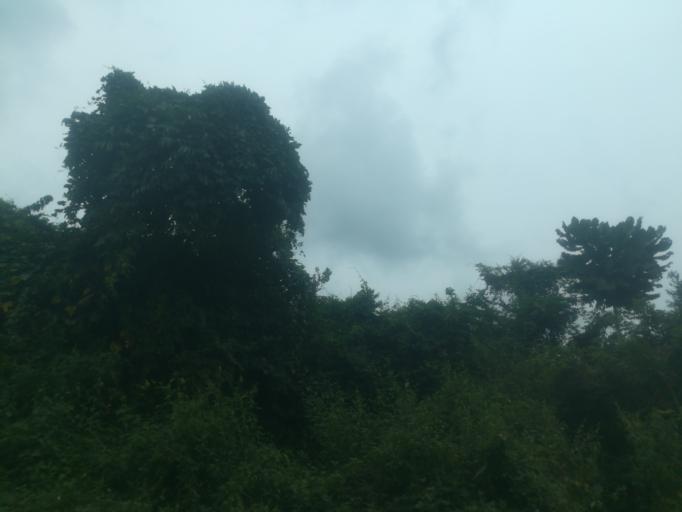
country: NG
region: Ogun
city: Ayetoro
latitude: 7.1036
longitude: 3.1402
